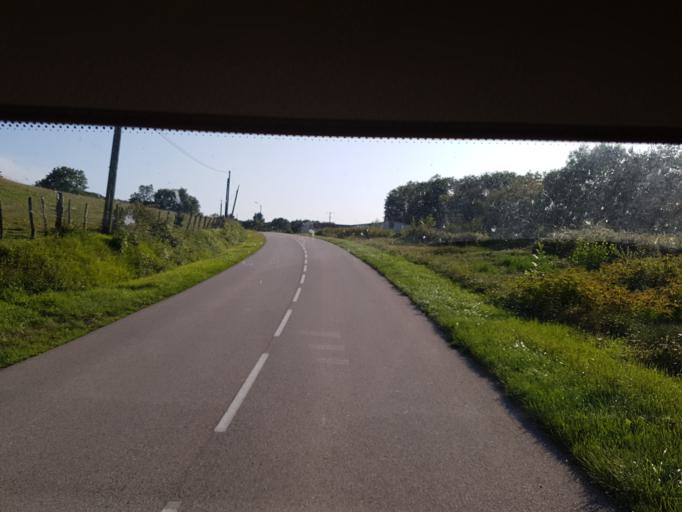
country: FR
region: Rhone-Alpes
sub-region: Departement de l'Ain
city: Neuville-sur-Ain
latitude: 46.1015
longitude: 5.3872
